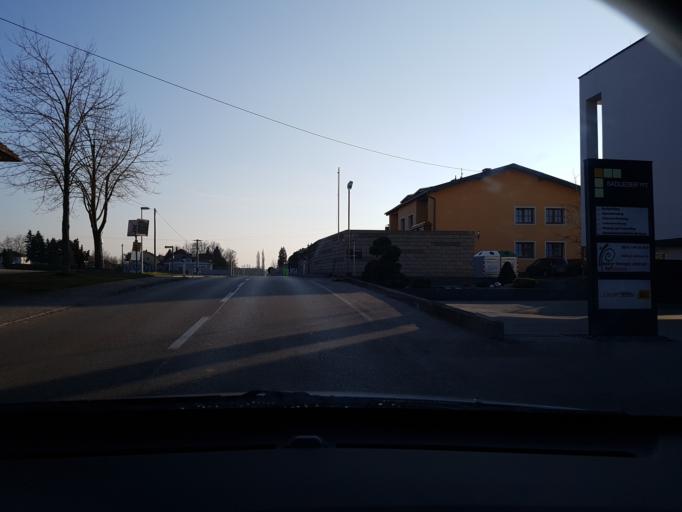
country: AT
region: Upper Austria
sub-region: Politischer Bezirk Linz-Land
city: Ansfelden
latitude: 48.1696
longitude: 14.2562
